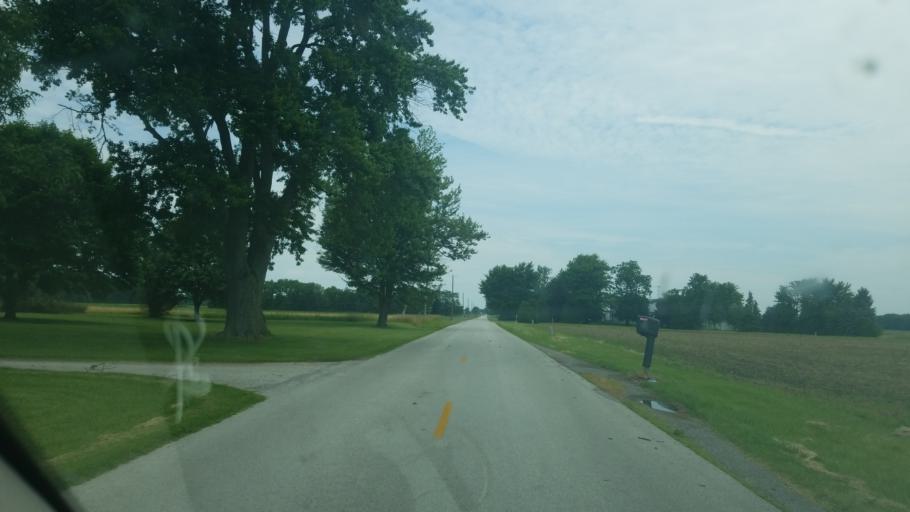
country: US
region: Ohio
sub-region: Seneca County
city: Fostoria
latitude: 41.0489
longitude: -83.4392
